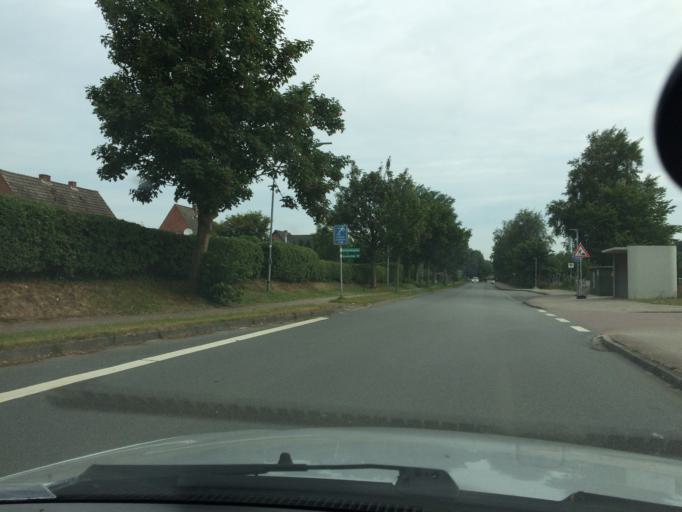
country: DE
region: Schleswig-Holstein
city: Oeversee
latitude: 54.6987
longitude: 9.4288
